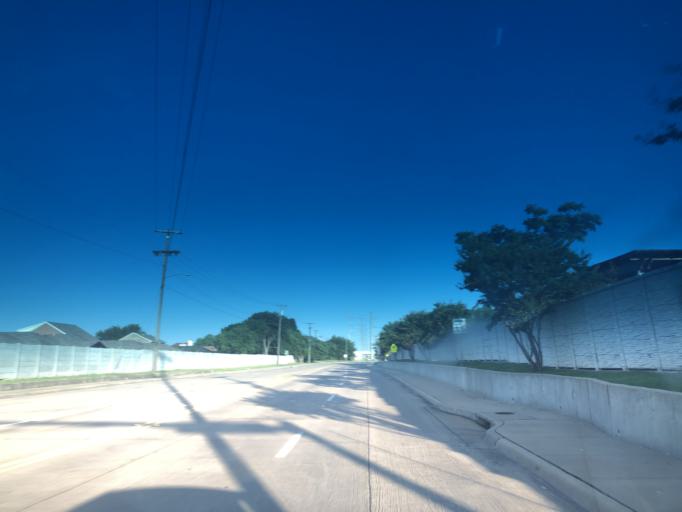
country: US
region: Texas
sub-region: Dallas County
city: Grand Prairie
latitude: 32.6983
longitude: -97.0186
